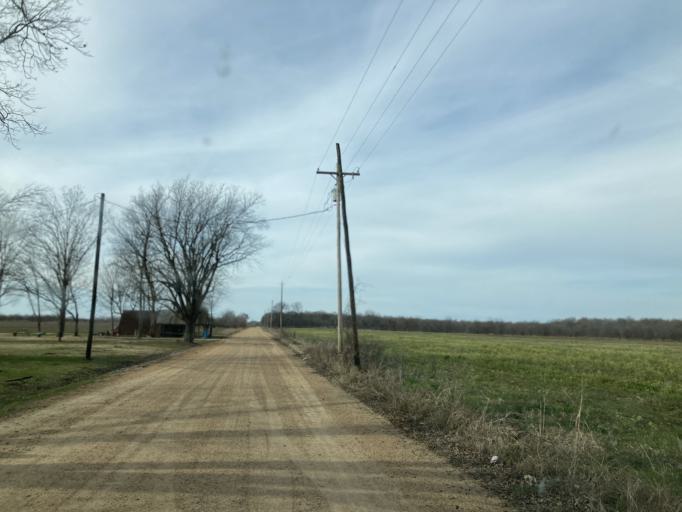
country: US
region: Mississippi
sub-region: Humphreys County
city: Belzoni
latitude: 33.1382
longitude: -90.6109
